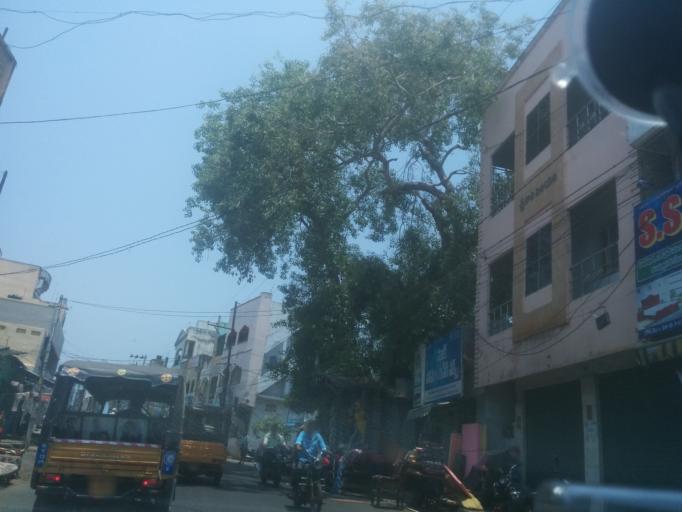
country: IN
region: Andhra Pradesh
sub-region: East Godavari
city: Rajahmundry
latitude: 17.0003
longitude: 81.7760
